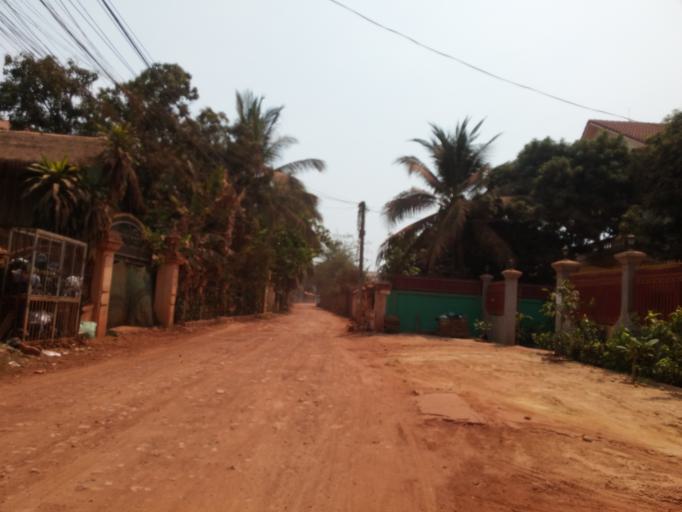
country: KH
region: Siem Reap
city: Siem Reap
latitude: 13.3707
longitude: 103.8476
